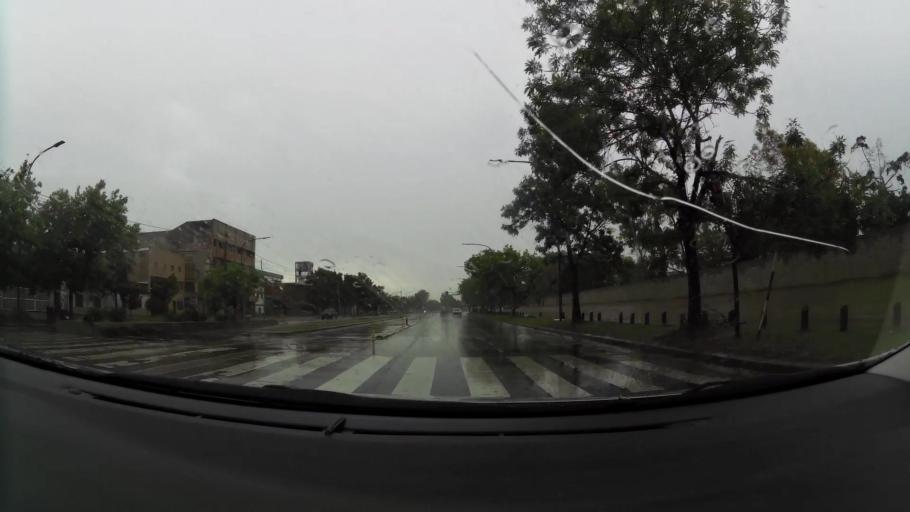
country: AR
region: Buenos Aires F.D.
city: Villa Lugano
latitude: -34.6536
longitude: -58.4353
